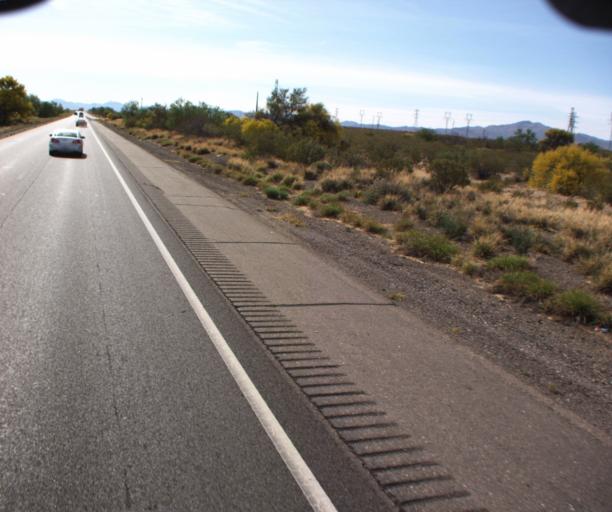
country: US
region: Arizona
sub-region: Pima County
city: Vail
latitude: 32.0613
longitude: -110.7735
